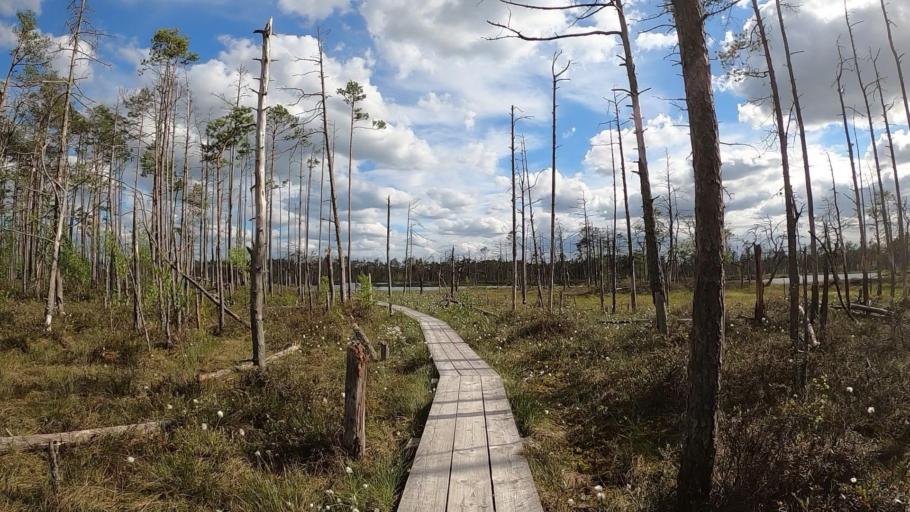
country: LV
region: Jurmala
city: Jurmala
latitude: 56.8520
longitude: 23.8143
